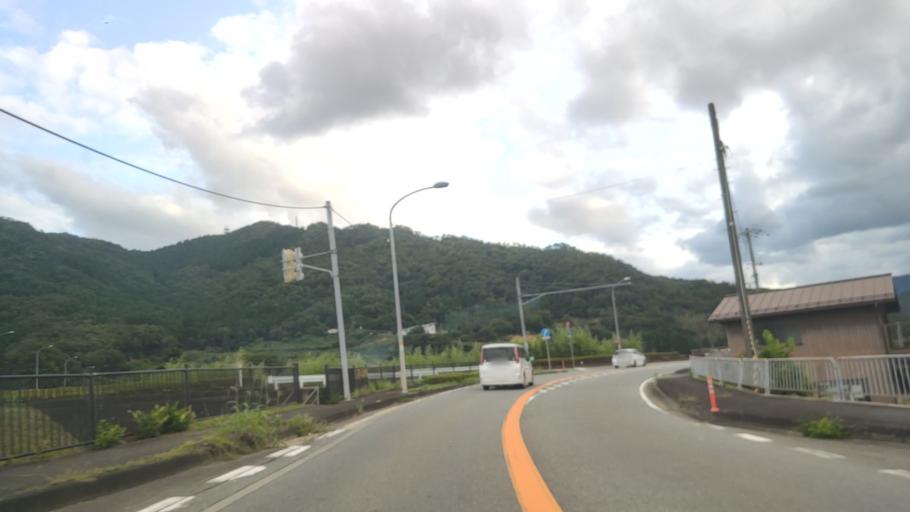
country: JP
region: Hyogo
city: Toyooka
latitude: 35.4204
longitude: 134.7908
